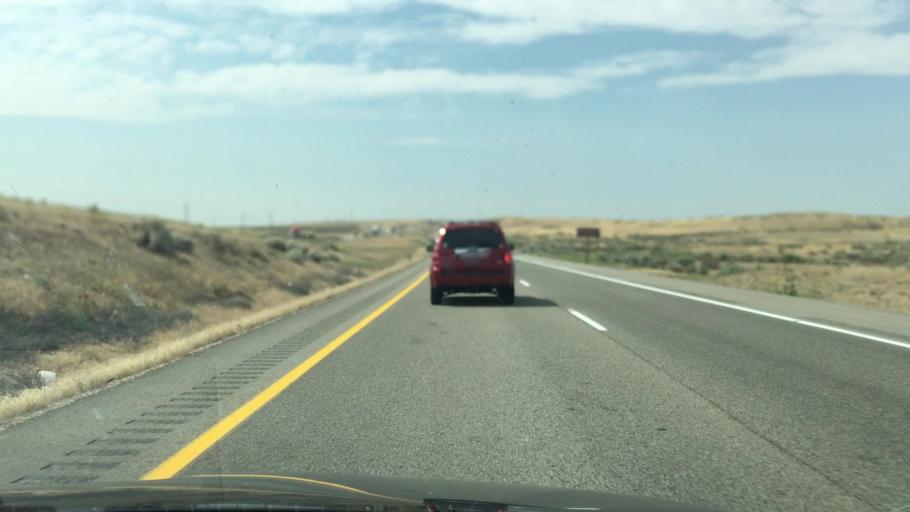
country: US
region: Idaho
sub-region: Ada County
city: Boise
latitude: 43.4566
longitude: -116.0844
